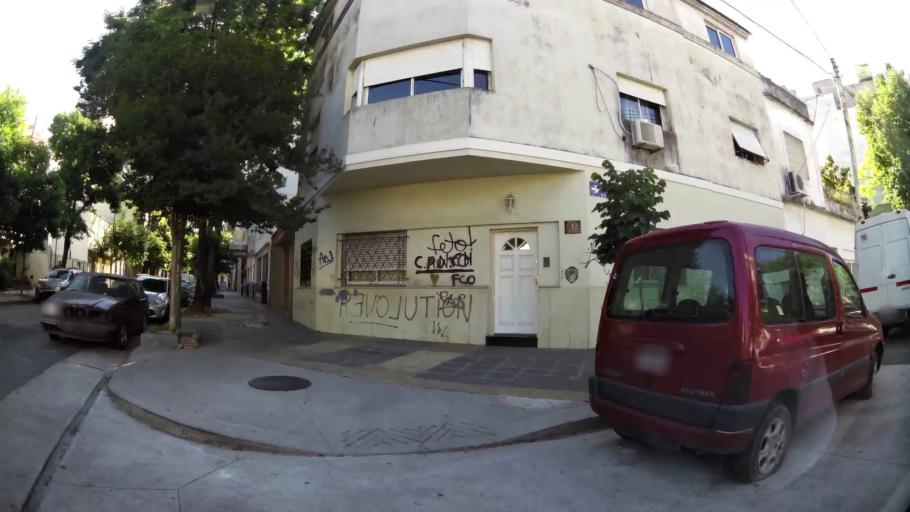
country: AR
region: Buenos Aires F.D.
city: Villa Santa Rita
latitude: -34.6198
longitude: -58.4598
